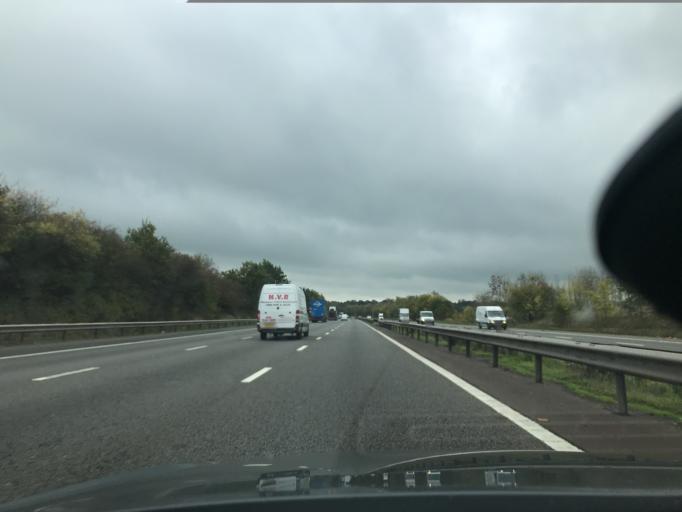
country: GB
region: England
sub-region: Warwickshire
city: Wroxall
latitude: 52.3150
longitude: -1.7148
